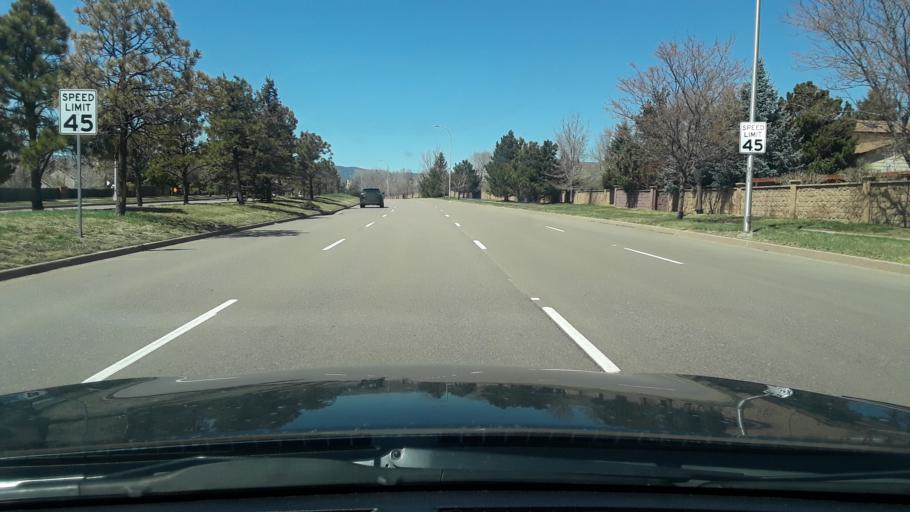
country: US
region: Colorado
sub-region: El Paso County
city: Black Forest
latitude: 38.9556
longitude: -104.7465
